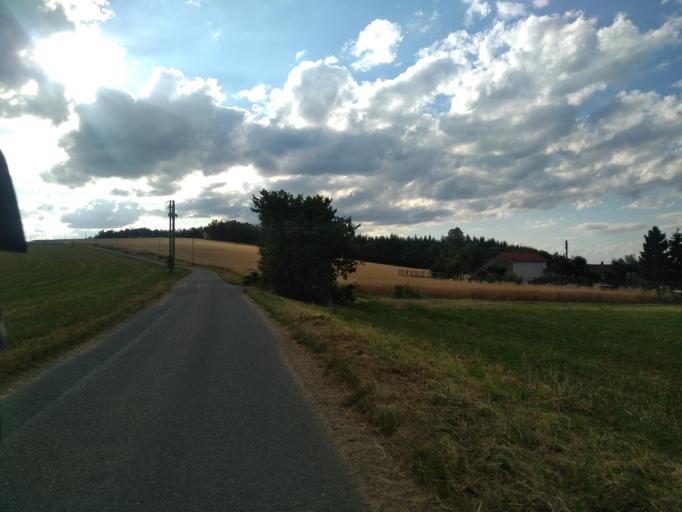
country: FR
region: Rhone-Alpes
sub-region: Departement de la Loire
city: Panissieres
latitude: 45.7429
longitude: 4.3357
